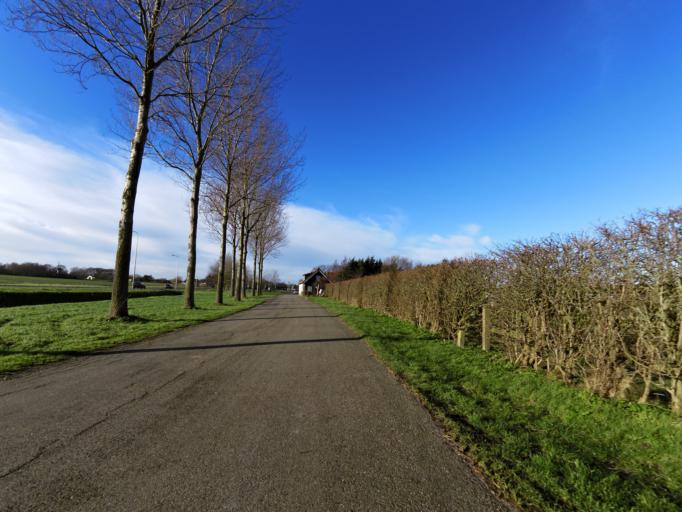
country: NL
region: South Holland
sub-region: Gemeente Hellevoetsluis
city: Nieuw-Helvoet
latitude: 51.8769
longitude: 4.0890
